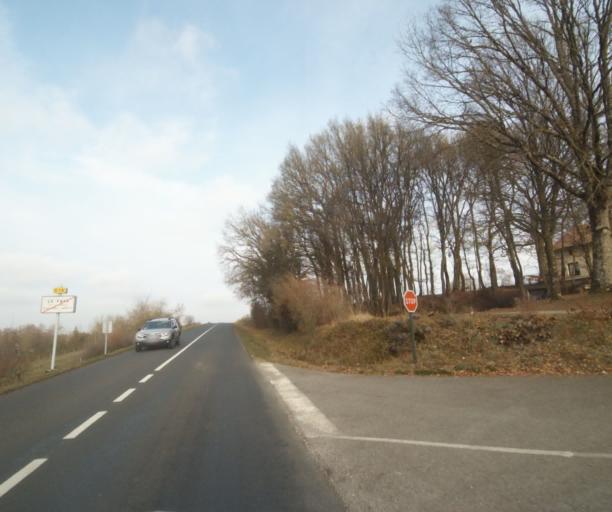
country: FR
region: Champagne-Ardenne
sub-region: Departement de la Marne
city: Sermaize-les-Bains
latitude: 48.7241
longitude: 4.9398
